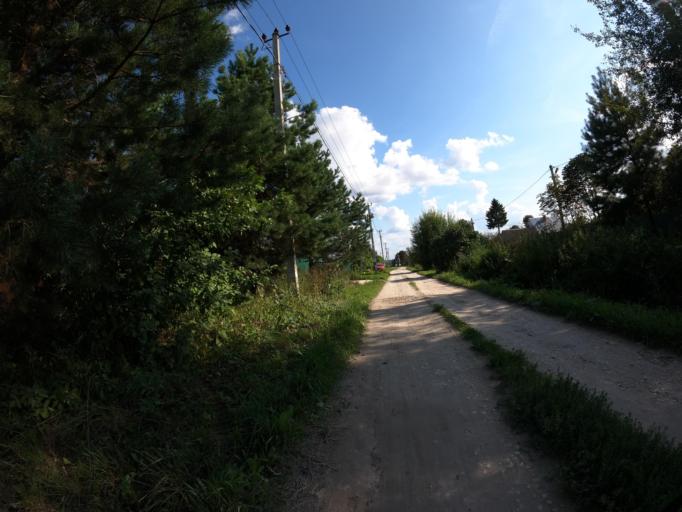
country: RU
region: Moskovskaya
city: Troitskoye
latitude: 55.2141
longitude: 38.4880
